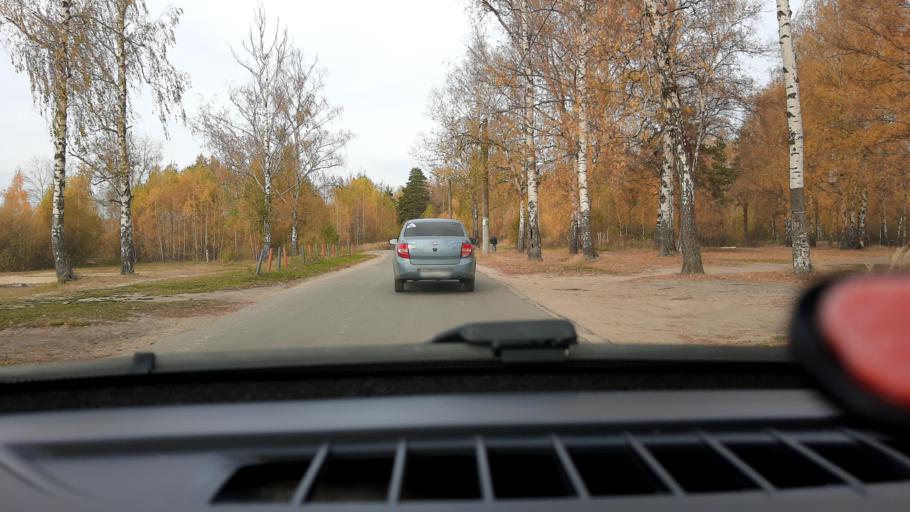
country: RU
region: Nizjnij Novgorod
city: Gorbatovka
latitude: 56.2938
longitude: 43.8346
